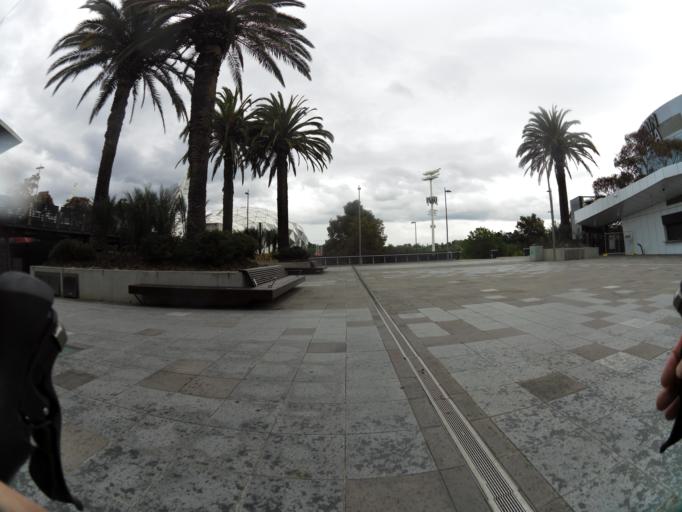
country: AU
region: Victoria
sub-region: Melbourne
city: East Melbourne
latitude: -37.8230
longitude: 144.9828
